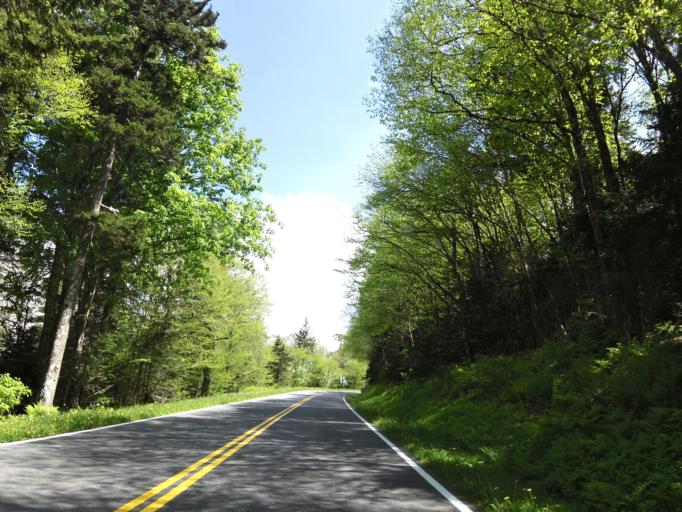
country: US
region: Tennessee
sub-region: Sevier County
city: Gatlinburg
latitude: 35.5937
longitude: -83.4620
